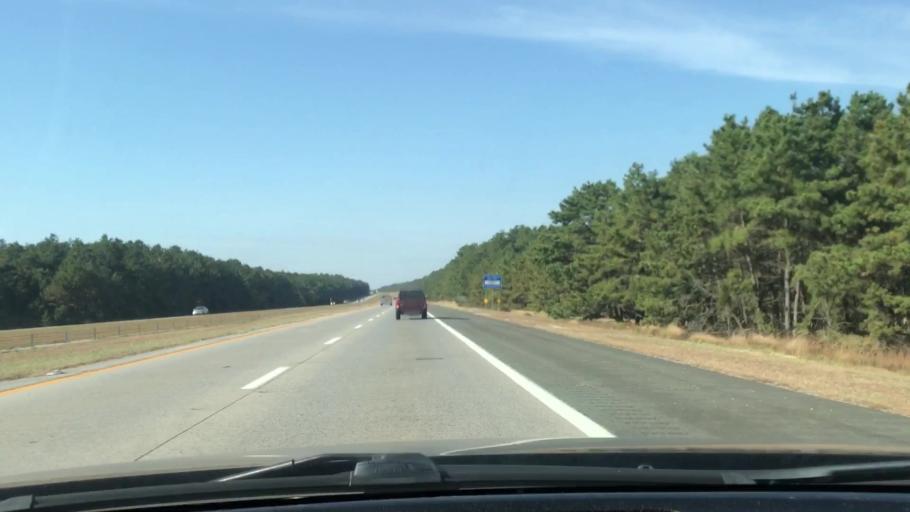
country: US
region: New York
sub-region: Suffolk County
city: East Quogue
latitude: 40.8754
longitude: -72.5821
